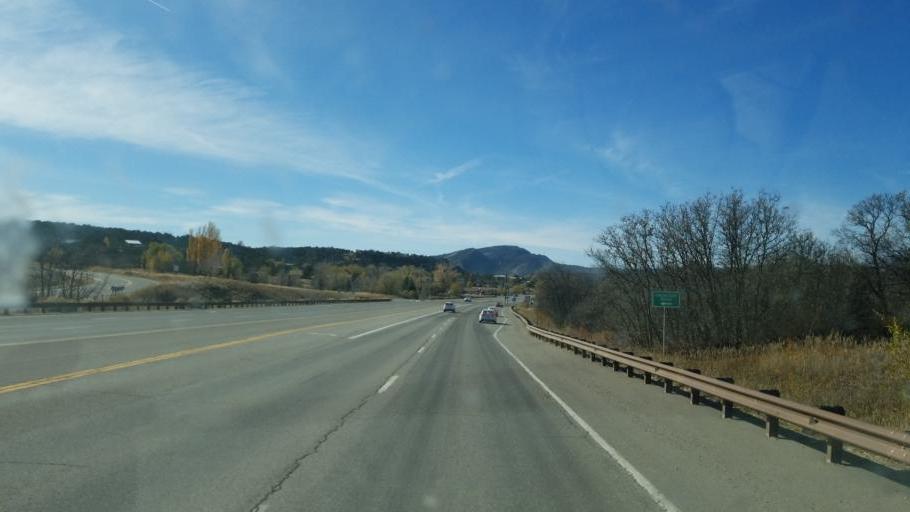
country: US
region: Colorado
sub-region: La Plata County
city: Durango
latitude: 37.2271
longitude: -107.8174
